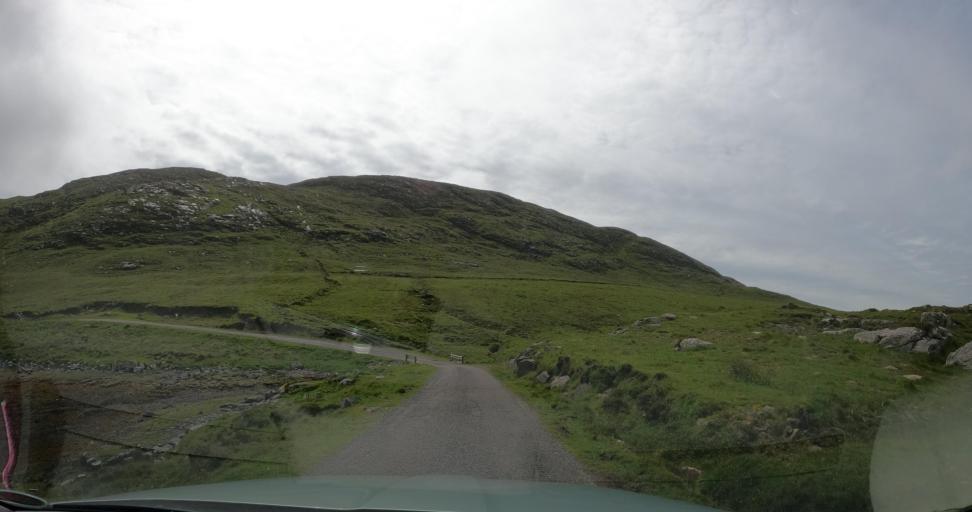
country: GB
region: Scotland
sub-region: Eilean Siar
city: Barra
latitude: 56.9399
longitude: -7.5421
